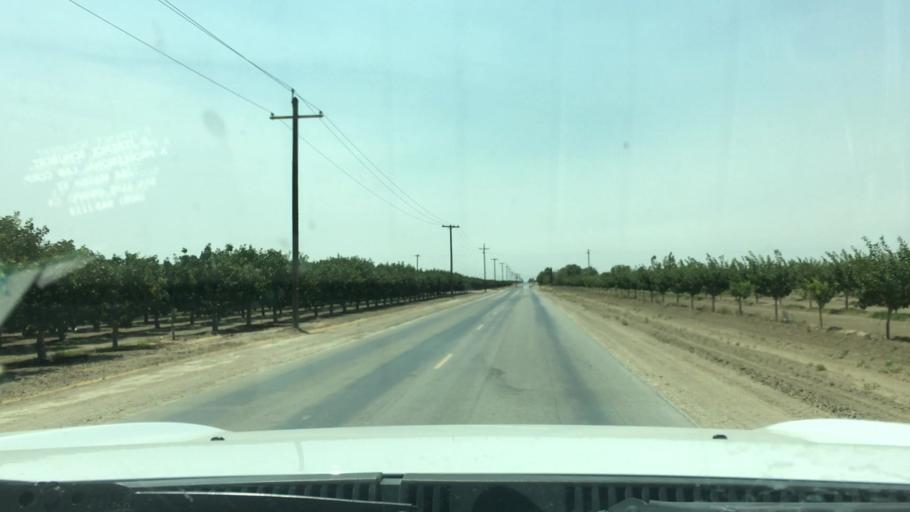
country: US
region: California
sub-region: Kern County
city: Wasco
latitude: 35.6906
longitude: -119.4374
